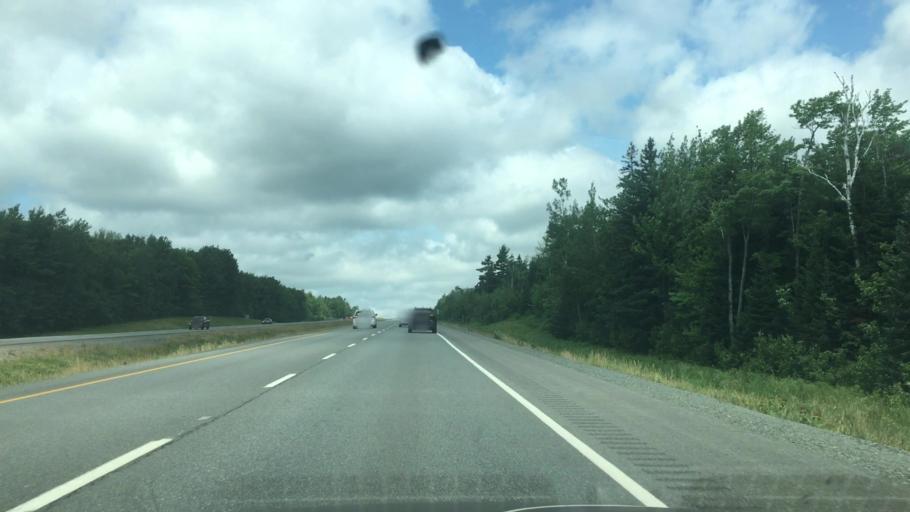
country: CA
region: Nova Scotia
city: Springhill
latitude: 45.7011
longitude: -64.0263
